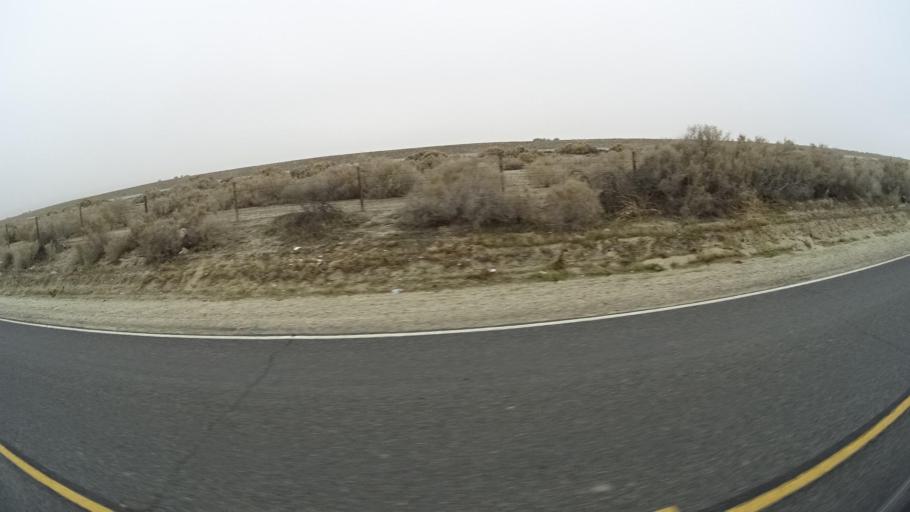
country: US
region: California
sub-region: Kern County
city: Buttonwillow
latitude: 35.3525
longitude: -119.4722
